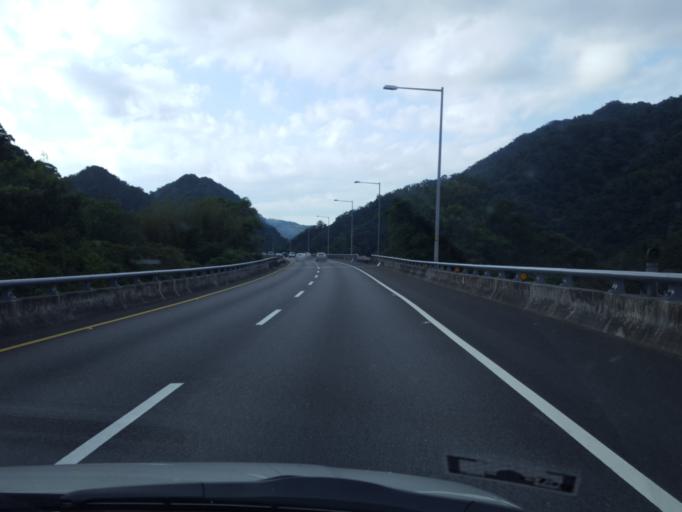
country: TW
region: Taipei
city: Taipei
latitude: 24.9794
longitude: 121.6753
